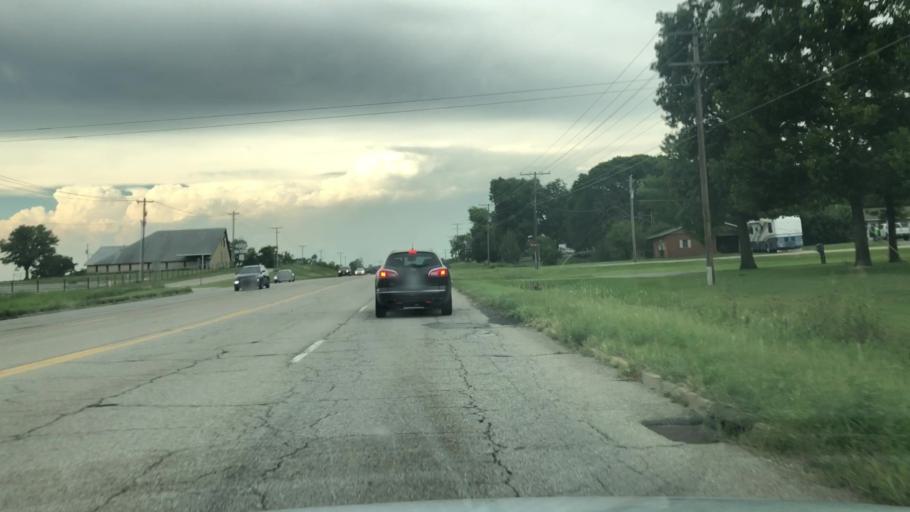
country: US
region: Oklahoma
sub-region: Washington County
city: Bartlesville
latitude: 36.6930
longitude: -95.9350
